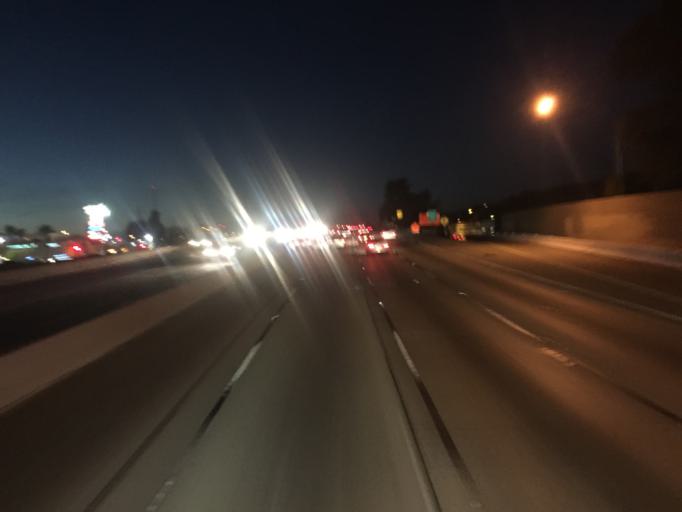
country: US
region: California
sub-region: Los Angeles County
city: Burbank
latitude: 34.1902
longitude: -118.3253
